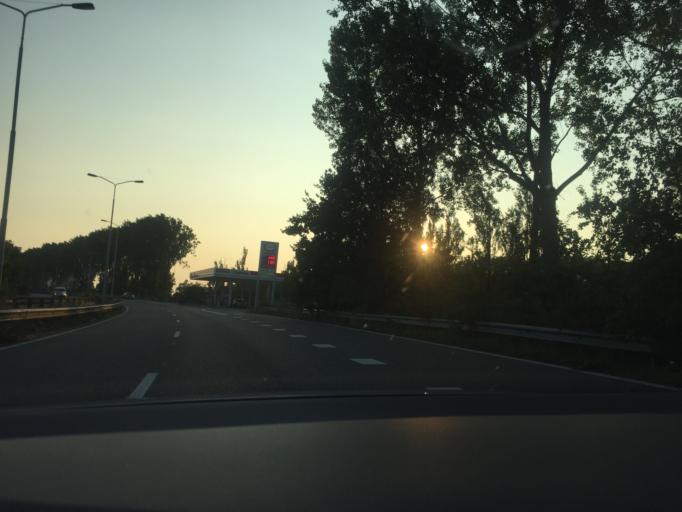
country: NL
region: North Holland
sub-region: Gemeente Zaanstad
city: Zaandam
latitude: 52.4552
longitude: 4.8331
